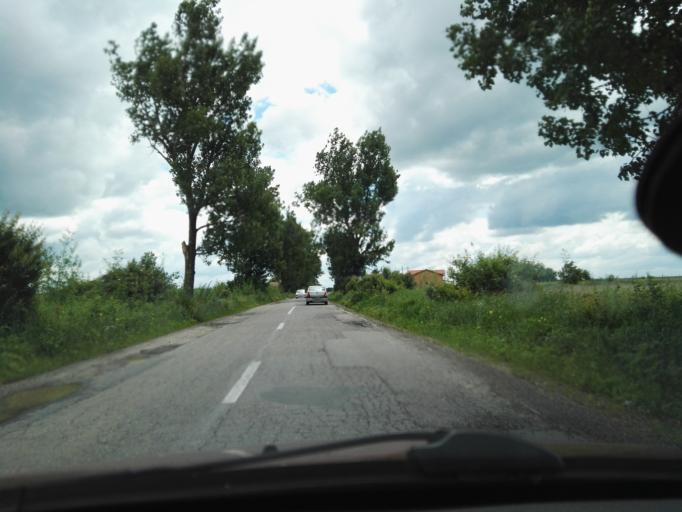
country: RO
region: Giurgiu
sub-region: Comuna Comana
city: Gradistea
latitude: 44.2272
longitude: 26.1391
